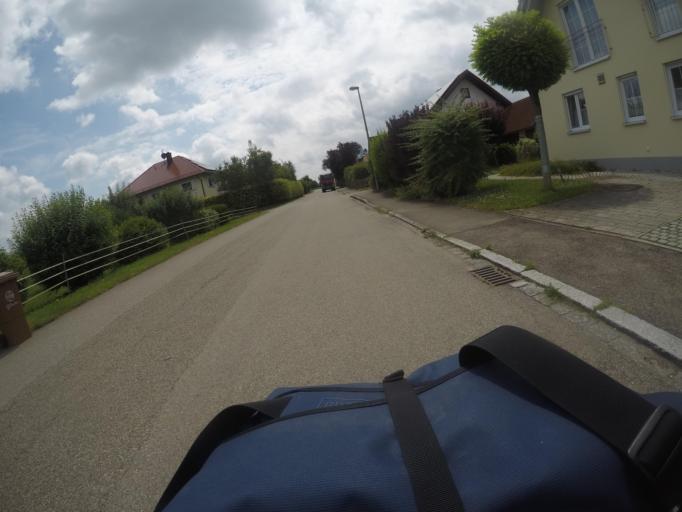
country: DE
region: Bavaria
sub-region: Swabia
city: Fellheim
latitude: 48.0736
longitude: 10.1563
